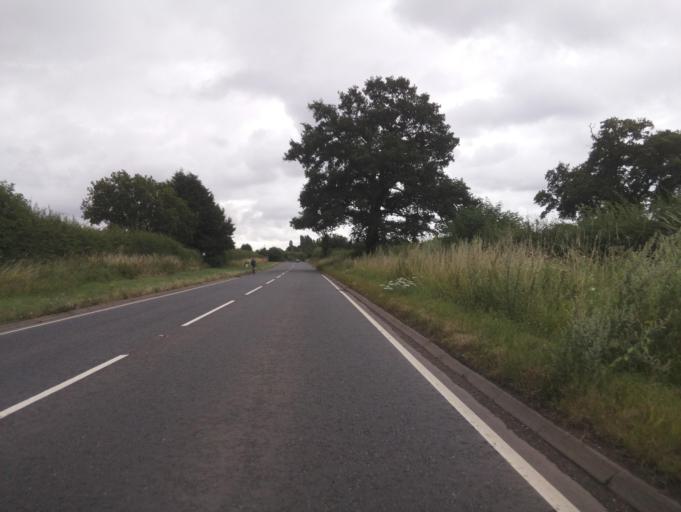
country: GB
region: England
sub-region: Worcestershire
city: Fernhill Heath
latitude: 52.2339
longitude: -2.1720
